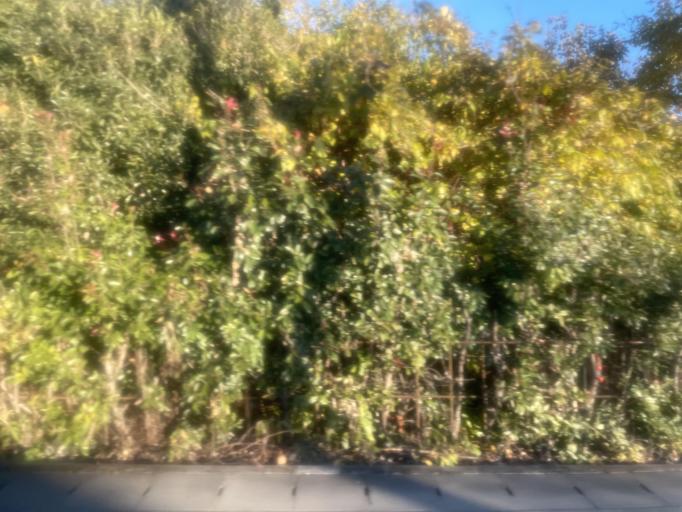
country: JP
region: Saitama
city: Yorii
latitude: 36.1080
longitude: 139.1988
